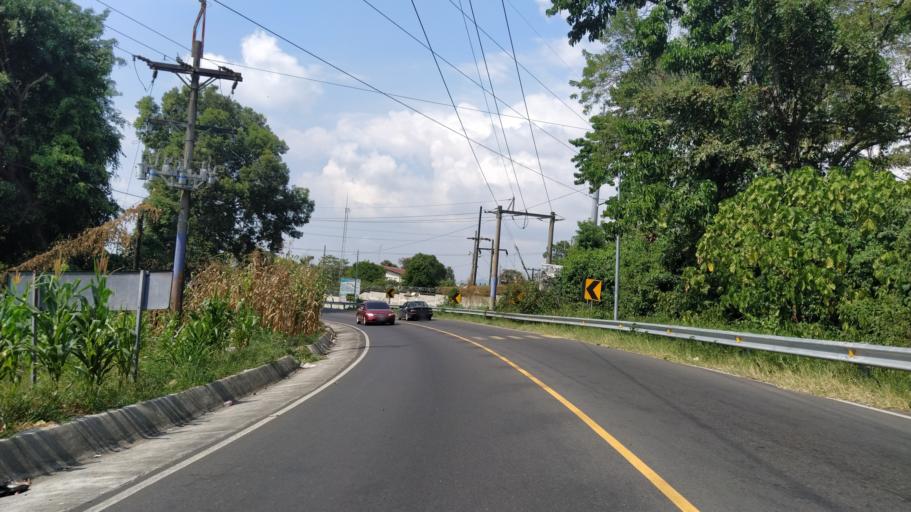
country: GT
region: Retalhuleu
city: San Felipe
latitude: 14.6208
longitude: -91.5890
